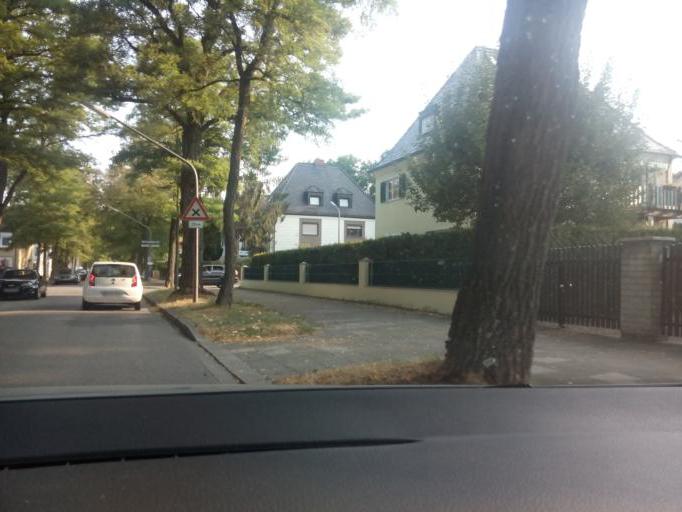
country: DE
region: Bavaria
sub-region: Upper Bavaria
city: Munich
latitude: 48.1122
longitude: 11.5989
